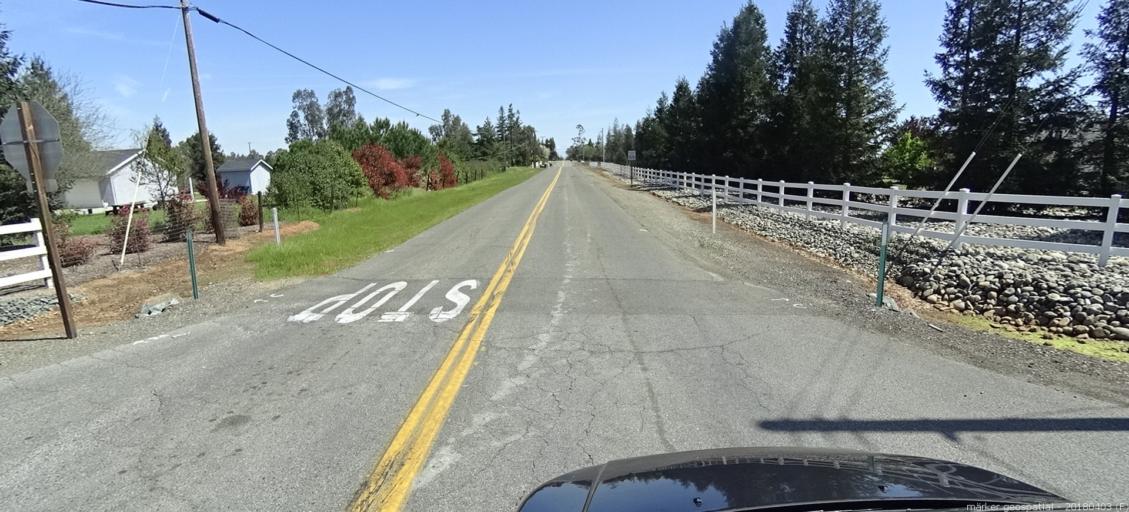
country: US
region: California
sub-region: Sacramento County
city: Wilton
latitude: 38.3797
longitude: -121.2422
